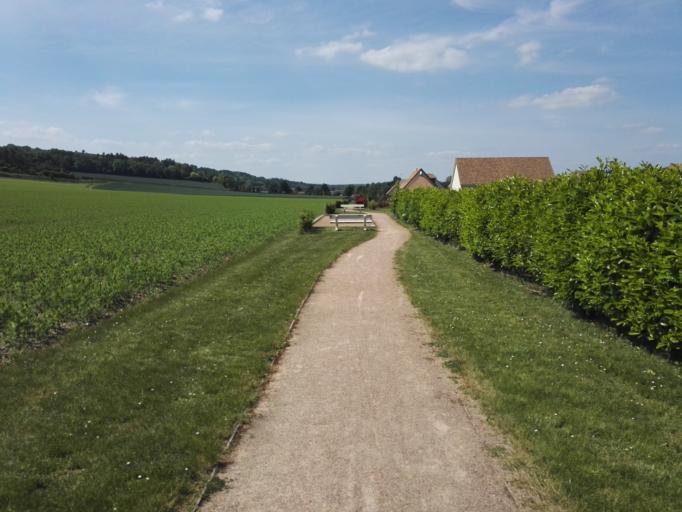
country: FR
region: Haute-Normandie
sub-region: Departement de l'Eure
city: Pacy-sur-Eure
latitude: 48.9939
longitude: 1.3824
